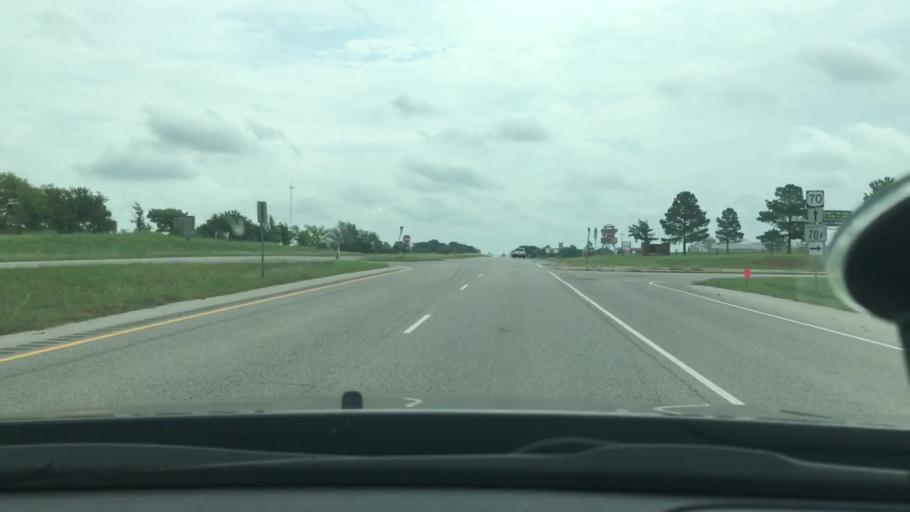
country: US
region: Oklahoma
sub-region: Carter County
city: Wilson
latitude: 34.1729
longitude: -97.4180
